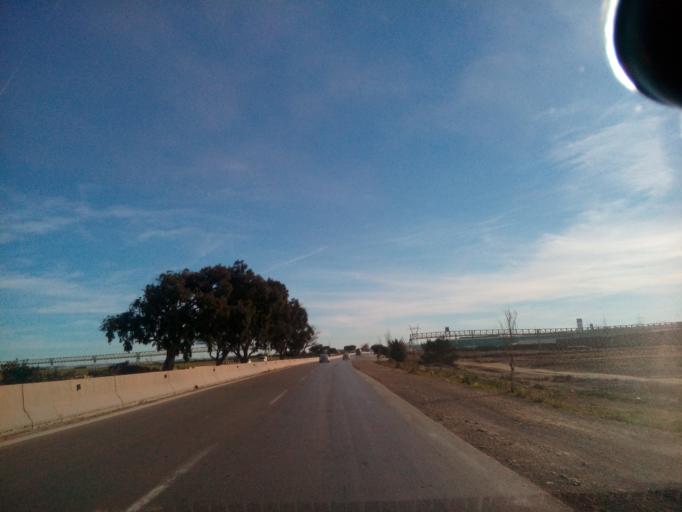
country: DZ
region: Oran
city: Ain el Bya
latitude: 35.7790
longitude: -0.2674
